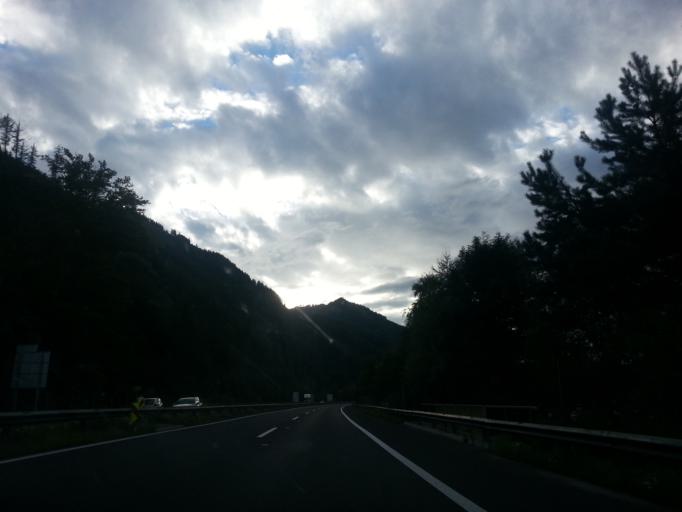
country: AT
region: Styria
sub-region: Politischer Bezirk Leoben
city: Mautern in Steiermark
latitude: 47.3970
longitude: 14.8039
